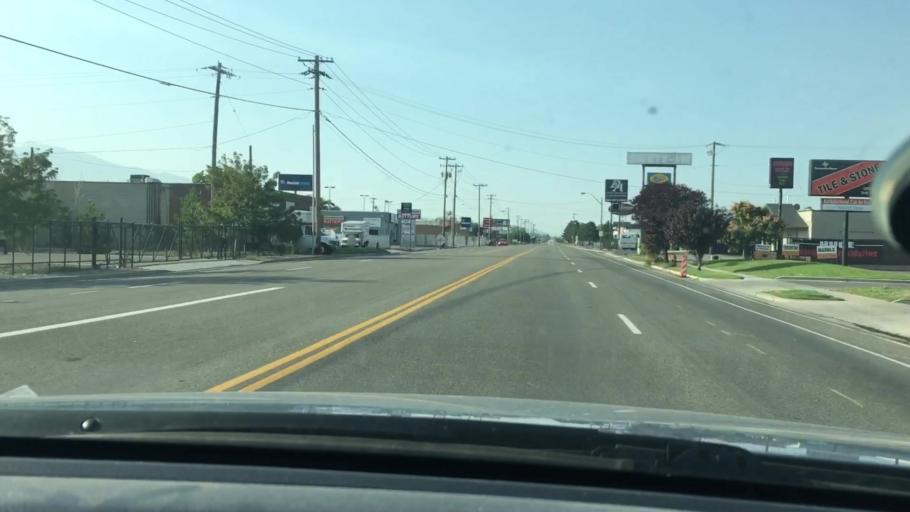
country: US
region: Utah
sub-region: Salt Lake County
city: South Salt Lake
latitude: 40.7122
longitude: -111.8998
